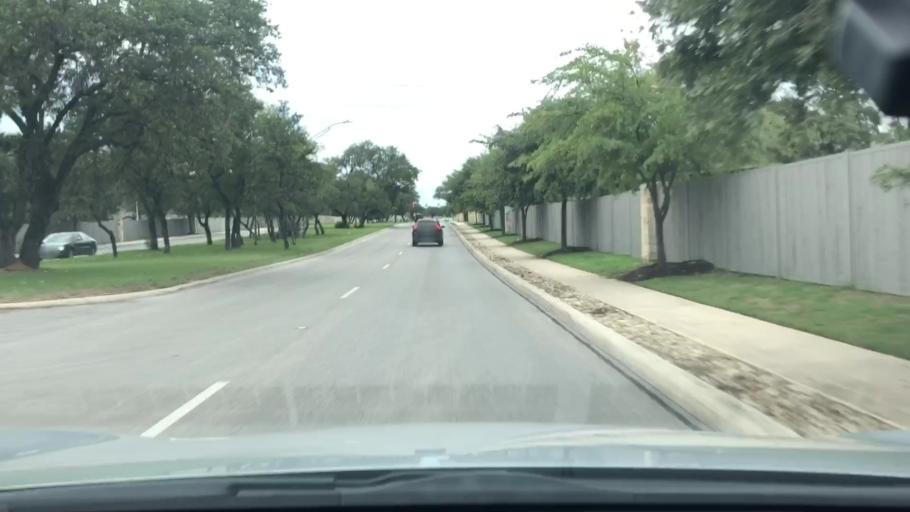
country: US
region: Texas
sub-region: Bexar County
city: Leon Valley
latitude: 29.4579
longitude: -98.6702
